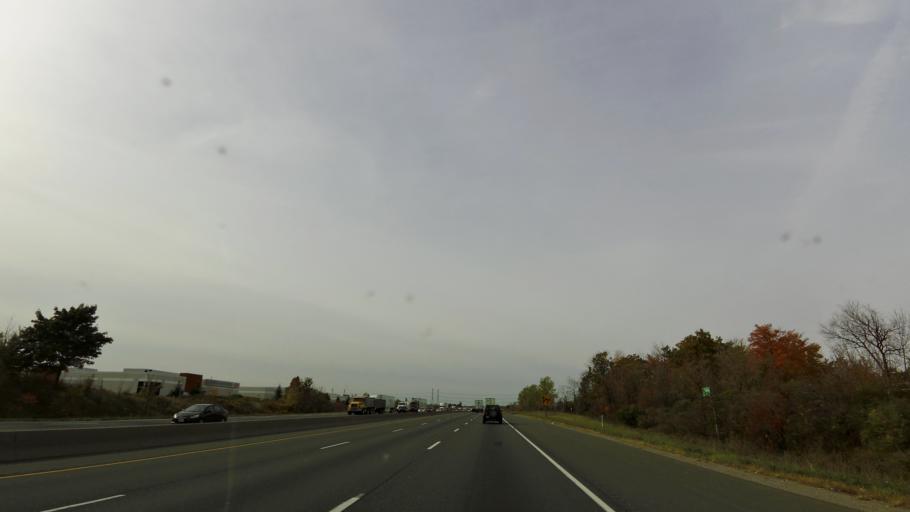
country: CA
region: Ontario
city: Brampton
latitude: 43.6014
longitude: -79.7759
